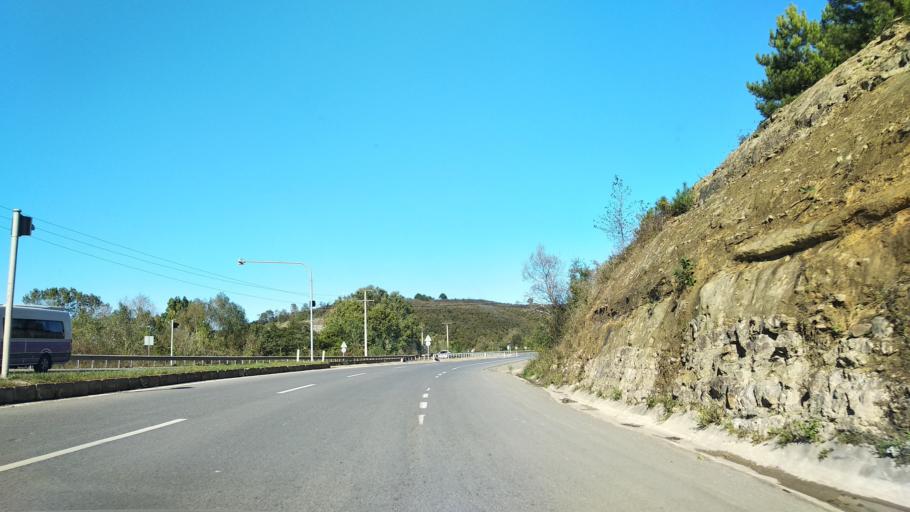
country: TR
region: Sakarya
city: Karasu
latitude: 41.0812
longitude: 30.6462
